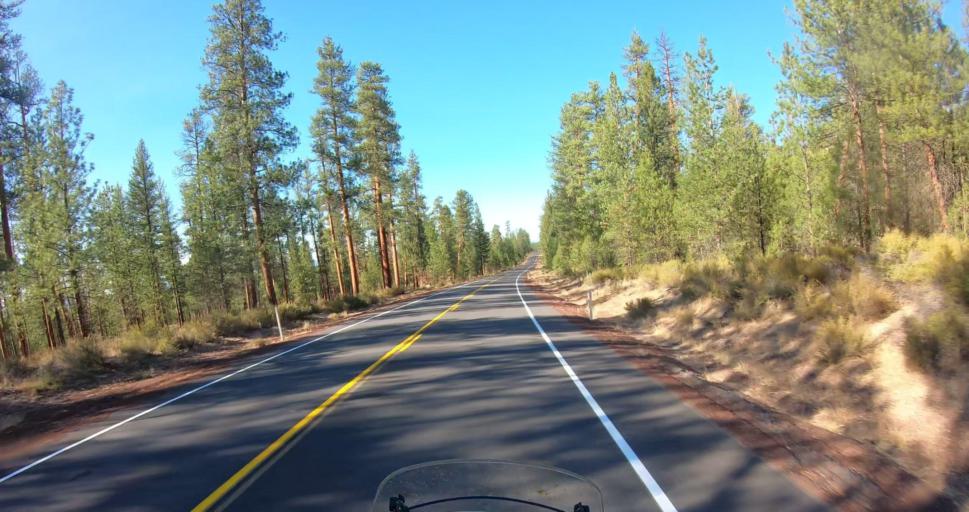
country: US
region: Oregon
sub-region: Deschutes County
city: La Pine
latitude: 43.5018
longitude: -121.4500
